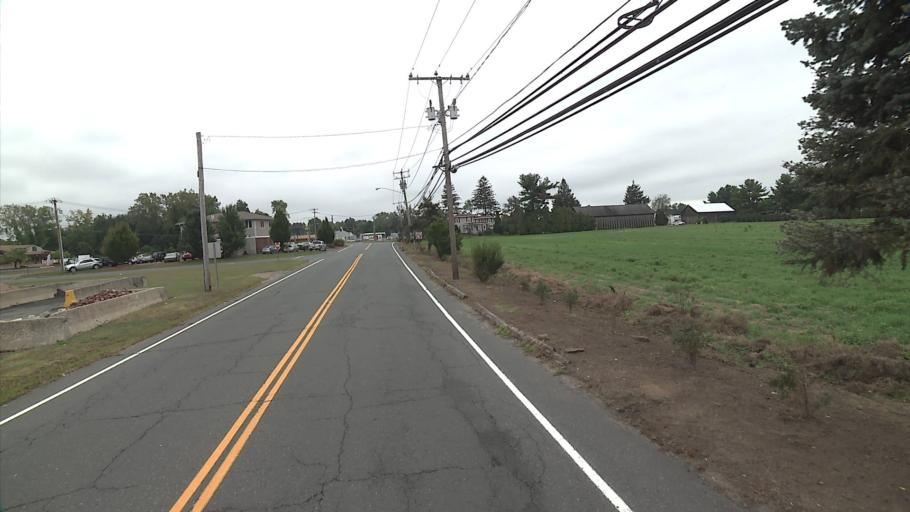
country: US
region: Connecticut
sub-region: Hartford County
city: Windsor Locks
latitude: 41.9150
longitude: -72.6140
